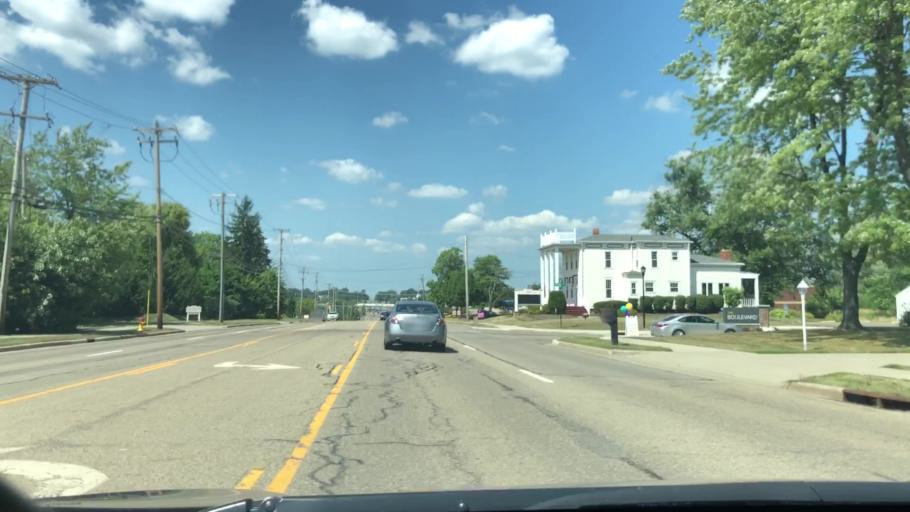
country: US
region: Ohio
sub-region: Summit County
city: Green
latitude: 40.9526
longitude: -81.4658
